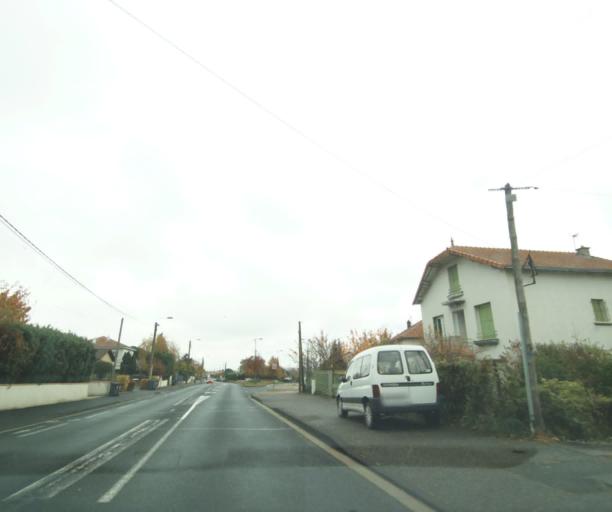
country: FR
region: Auvergne
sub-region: Departement du Puy-de-Dome
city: Aubiere
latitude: 45.7478
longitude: 3.1012
